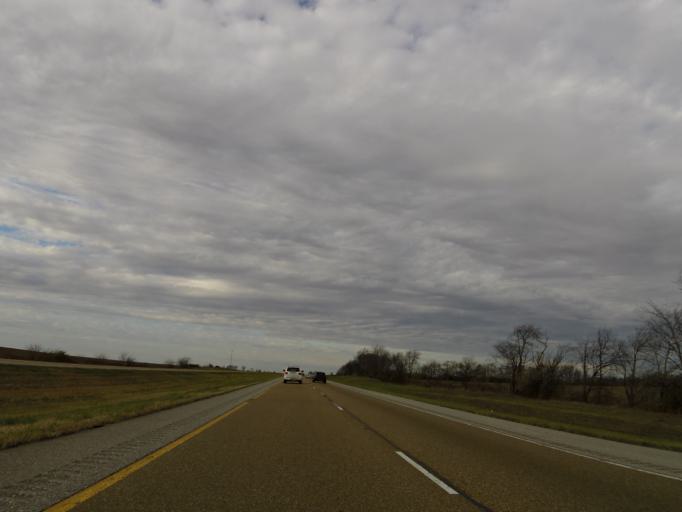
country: US
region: Illinois
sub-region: Clinton County
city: Wamac
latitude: 38.3901
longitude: -89.2349
